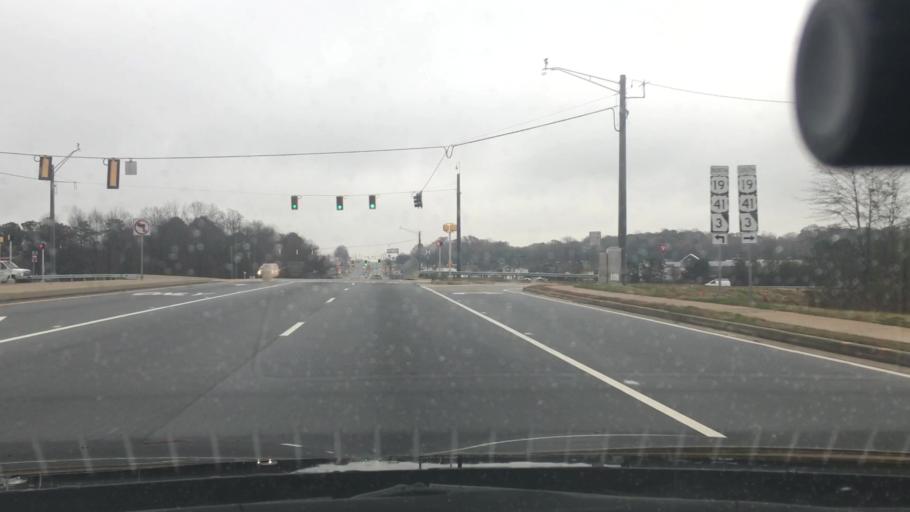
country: US
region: Georgia
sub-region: Spalding County
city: Experiment
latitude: 33.2474
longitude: -84.2979
